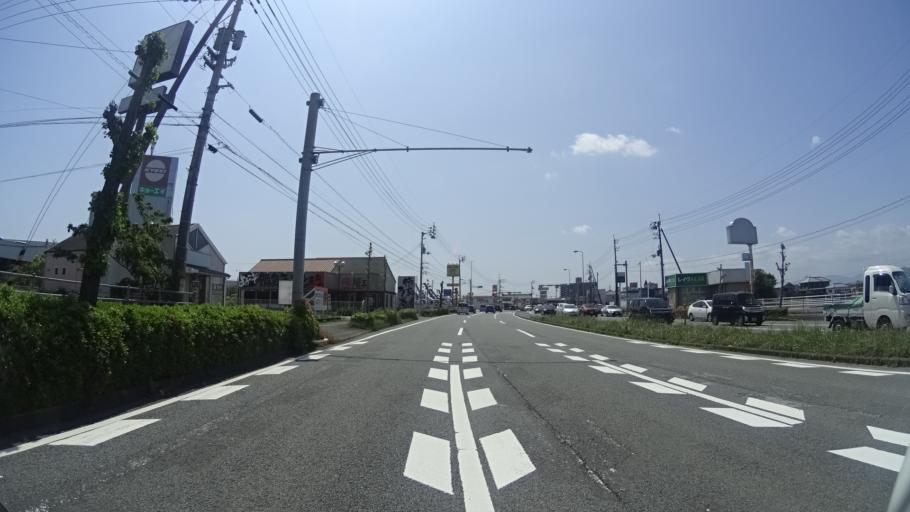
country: JP
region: Tokushima
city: Tokushima-shi
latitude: 34.1227
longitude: 134.5779
